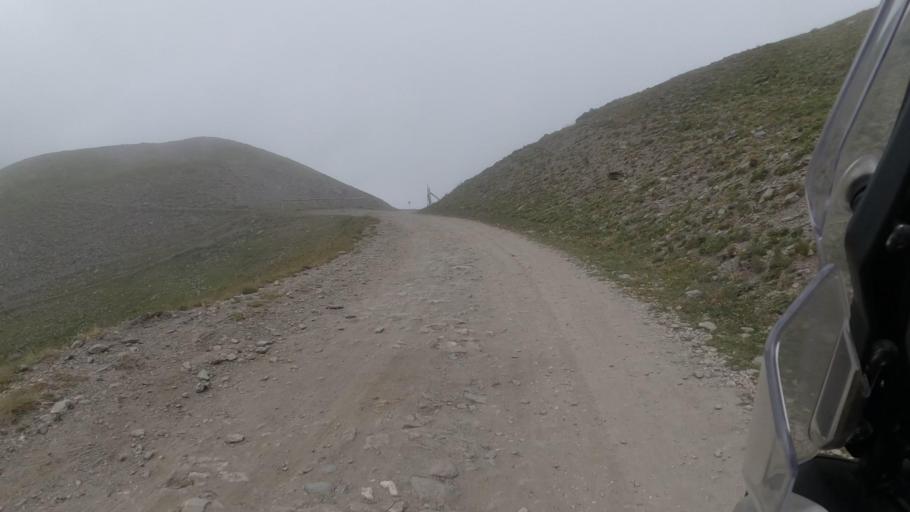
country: IT
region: Piedmont
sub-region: Provincia di Torino
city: Exilles
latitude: 45.0648
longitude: 6.9511
